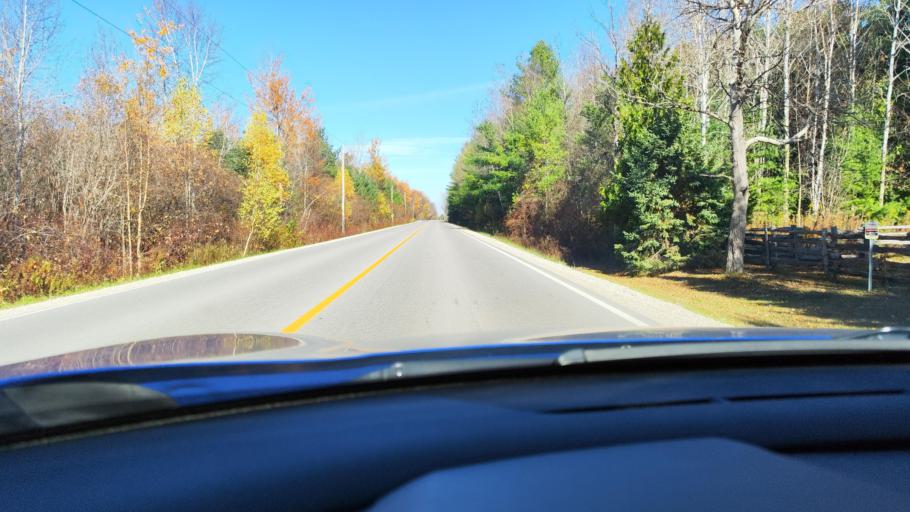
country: CA
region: Ontario
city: Wasaga Beach
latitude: 44.4064
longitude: -80.0592
